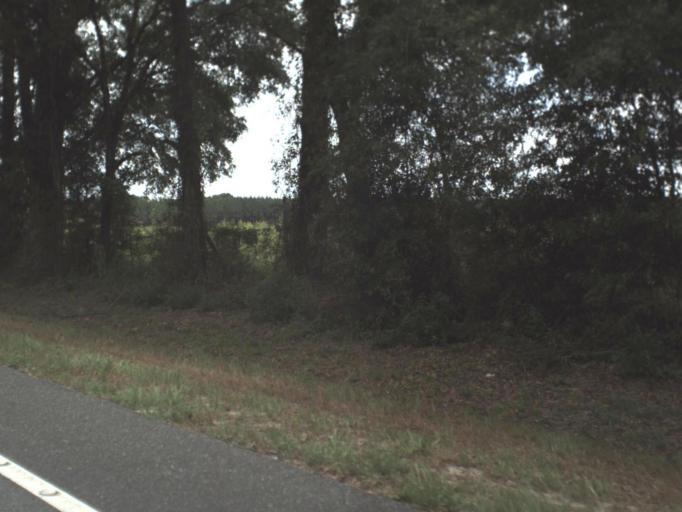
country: US
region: Florida
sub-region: Suwannee County
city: Wellborn
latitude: 29.9885
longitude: -82.8719
